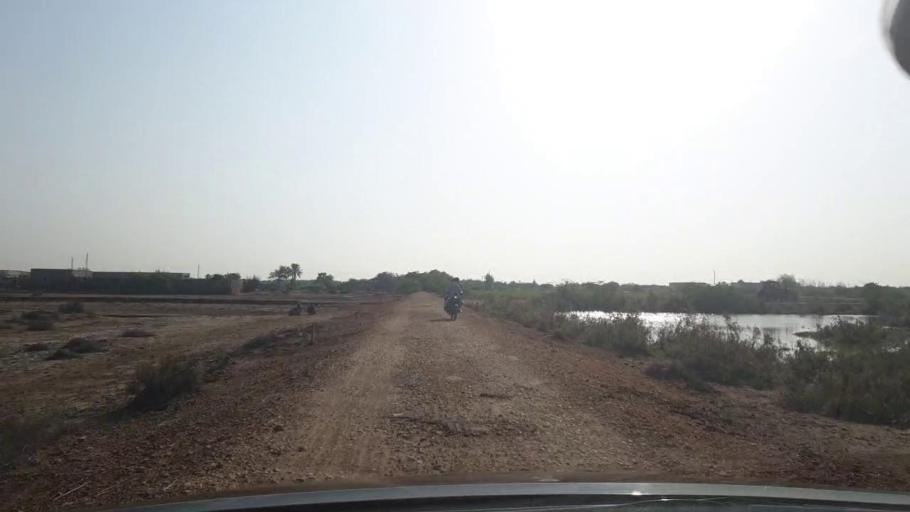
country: PK
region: Sindh
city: Tando Bago
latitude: 24.6510
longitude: 69.1360
